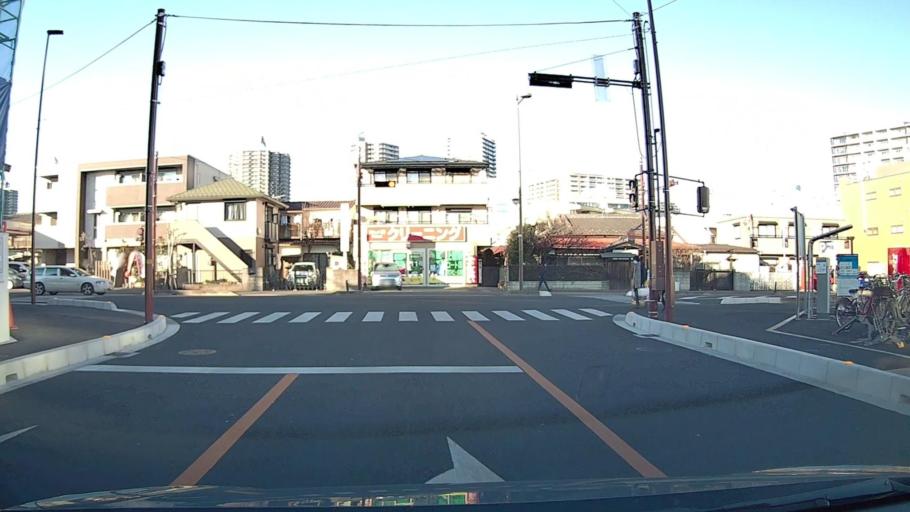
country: JP
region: Saitama
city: Tokorozawa
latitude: 35.7865
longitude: 139.4698
